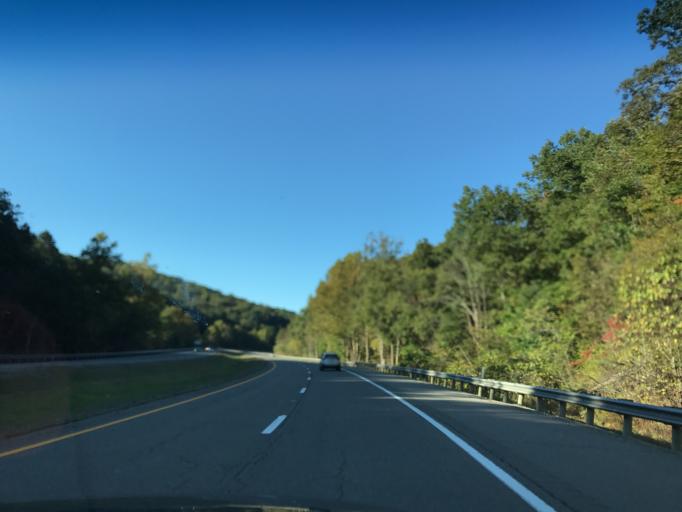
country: US
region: Ohio
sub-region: Washington County
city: Newport
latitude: 39.2580
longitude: -81.2936
